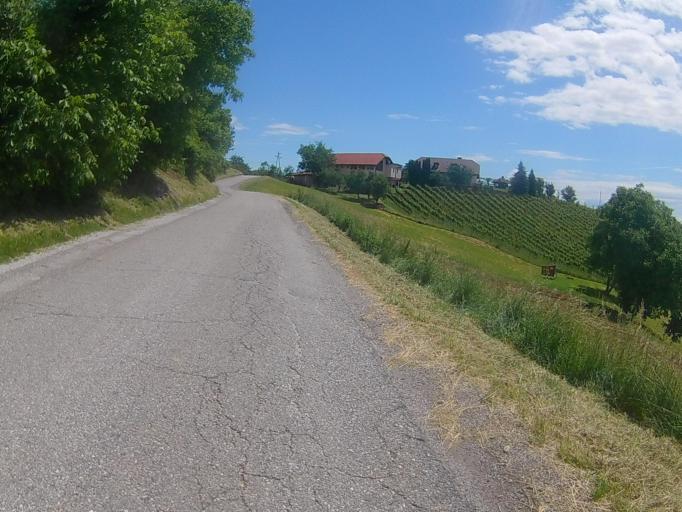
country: SI
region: Duplek
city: Zgornji Duplek
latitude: 46.5547
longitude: 15.7210
